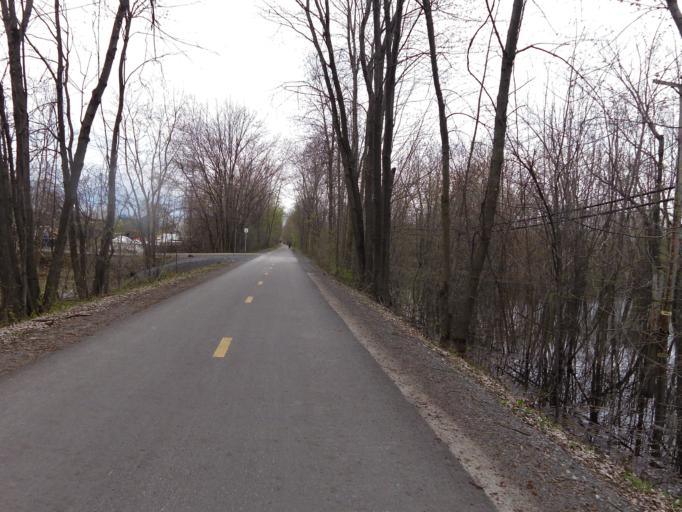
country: CA
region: Quebec
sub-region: Laurentides
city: Sainte-Marthe-sur-le-Lac
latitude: 45.5084
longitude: -73.9701
